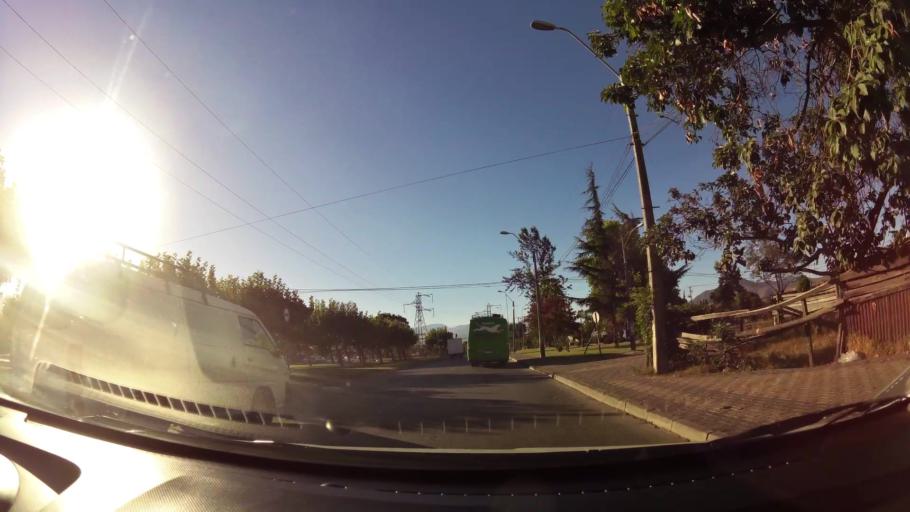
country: CL
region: O'Higgins
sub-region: Provincia de Cachapoal
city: Rancagua
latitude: -34.1737
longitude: -70.7140
